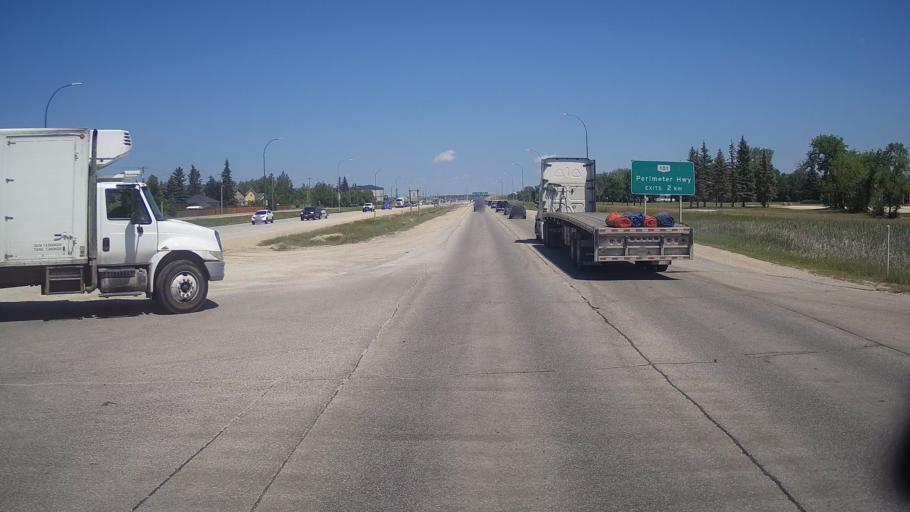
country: CA
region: Manitoba
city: Winnipeg
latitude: 49.9376
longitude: -97.0387
